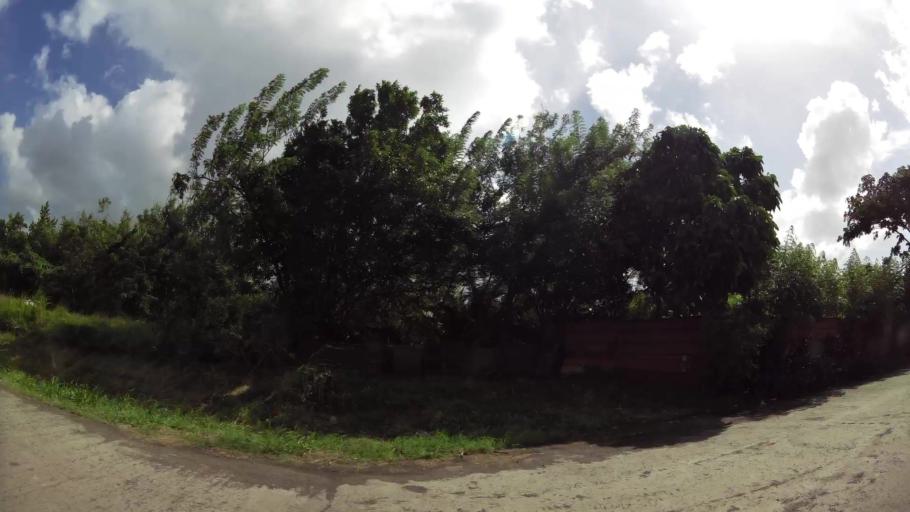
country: MQ
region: Martinique
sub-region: Martinique
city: Fort-de-France
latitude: 14.5993
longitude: -61.0507
